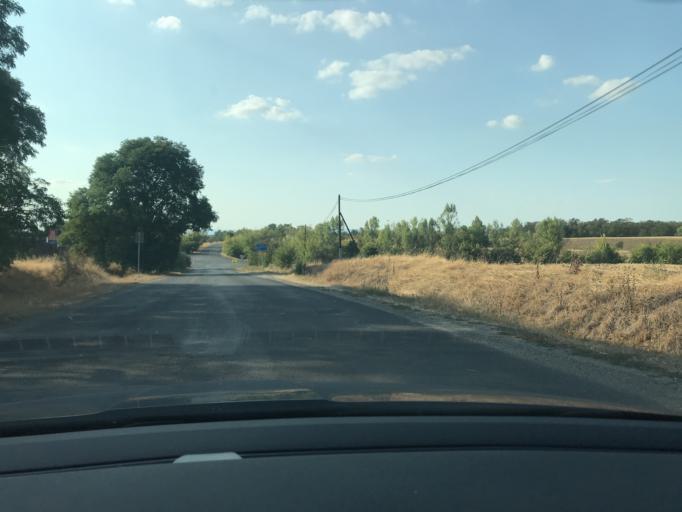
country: CZ
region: Ustecky
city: Postoloprty
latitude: 50.3642
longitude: 13.6906
